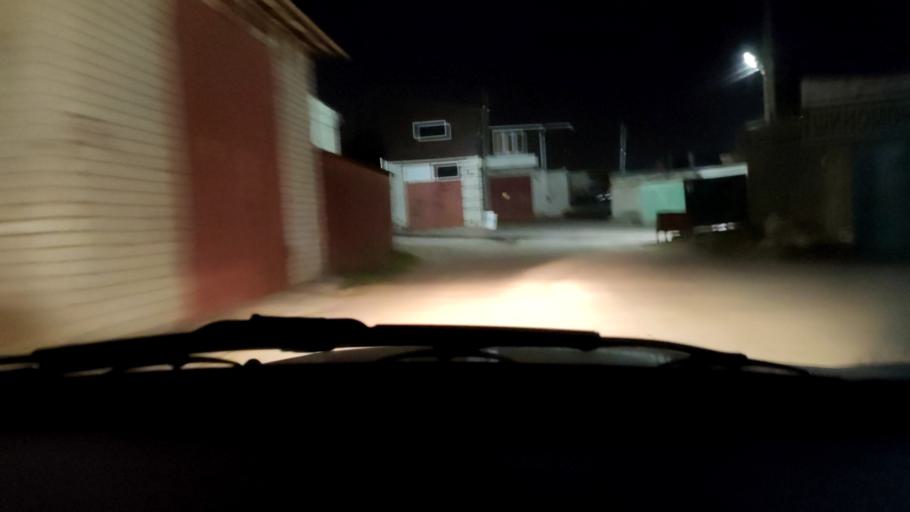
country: RU
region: Voronezj
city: Pridonskoy
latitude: 51.6412
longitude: 39.1153
